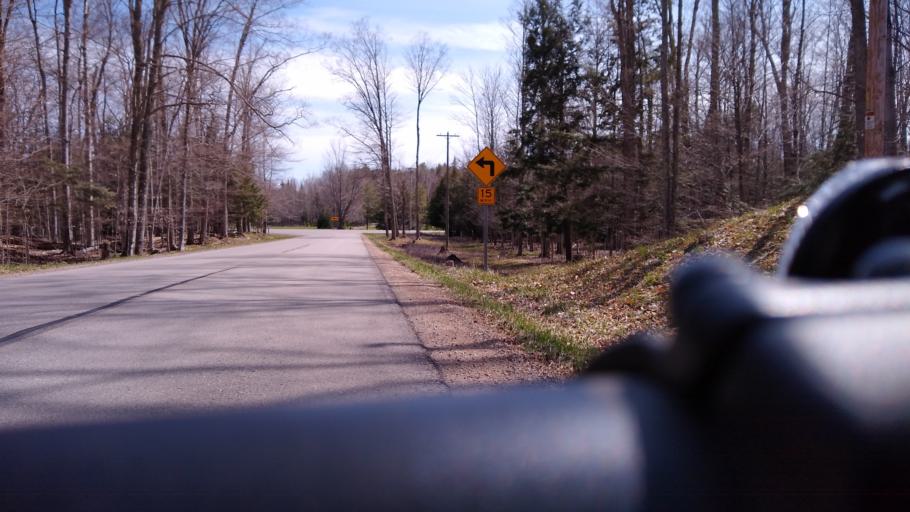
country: US
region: Michigan
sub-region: Delta County
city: Escanaba
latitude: 45.6968
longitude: -87.1629
